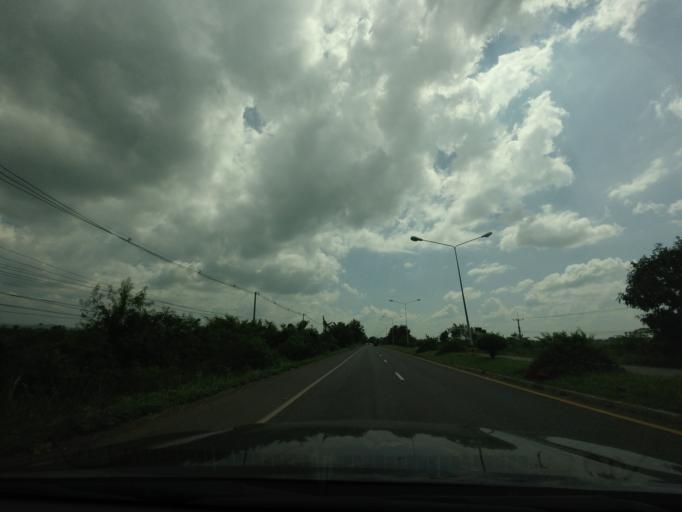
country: TH
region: Phetchabun
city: Nong Phai
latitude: 16.1890
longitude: 101.0889
